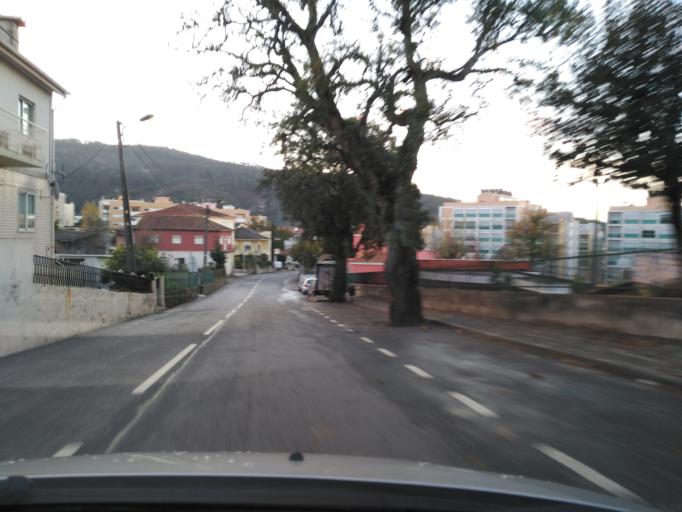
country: PT
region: Braga
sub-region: Braga
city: Braga
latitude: 41.5328
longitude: -8.4107
